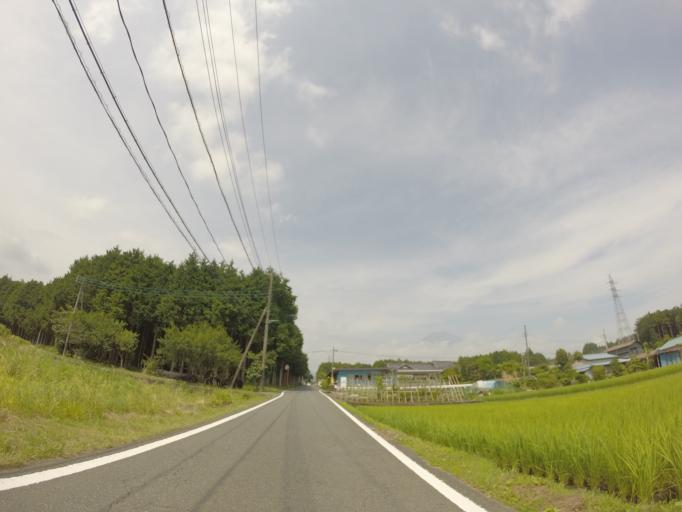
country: JP
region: Shizuoka
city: Fujinomiya
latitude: 35.2944
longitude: 138.5832
